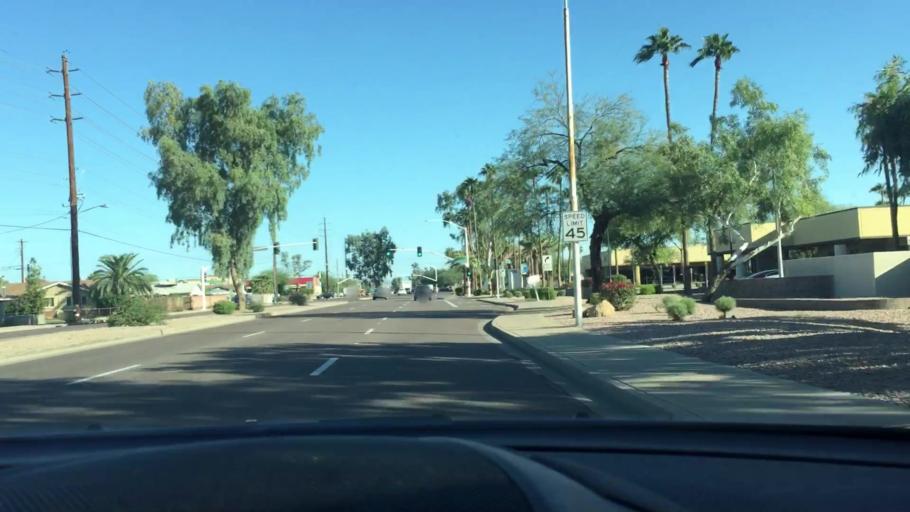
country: US
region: Arizona
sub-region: Maricopa County
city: Scottsdale
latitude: 33.4630
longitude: -111.9088
